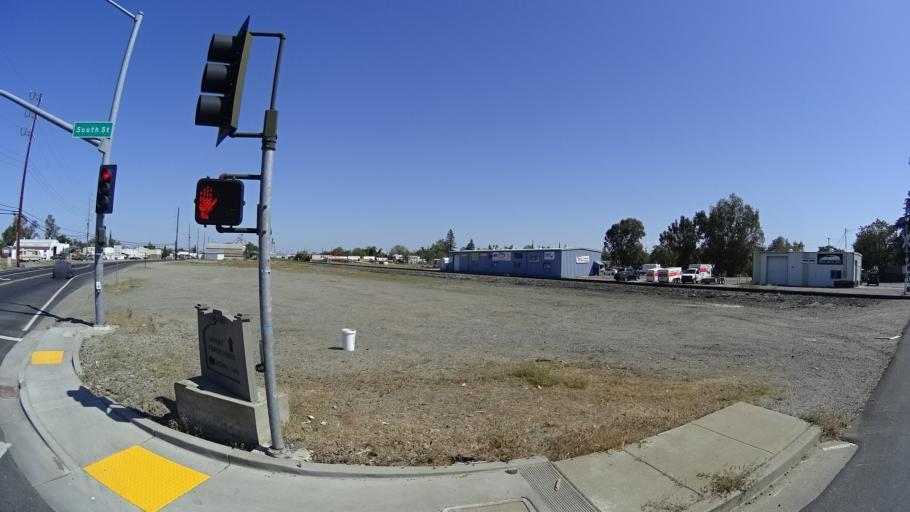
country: US
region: California
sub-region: Glenn County
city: Orland
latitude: 39.7403
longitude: -122.1972
